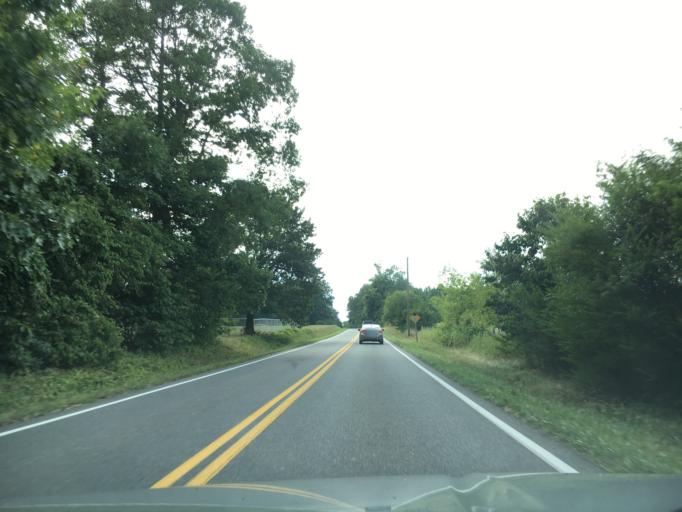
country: US
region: Virginia
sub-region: Campbell County
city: Rustburg
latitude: 37.2558
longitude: -79.1393
